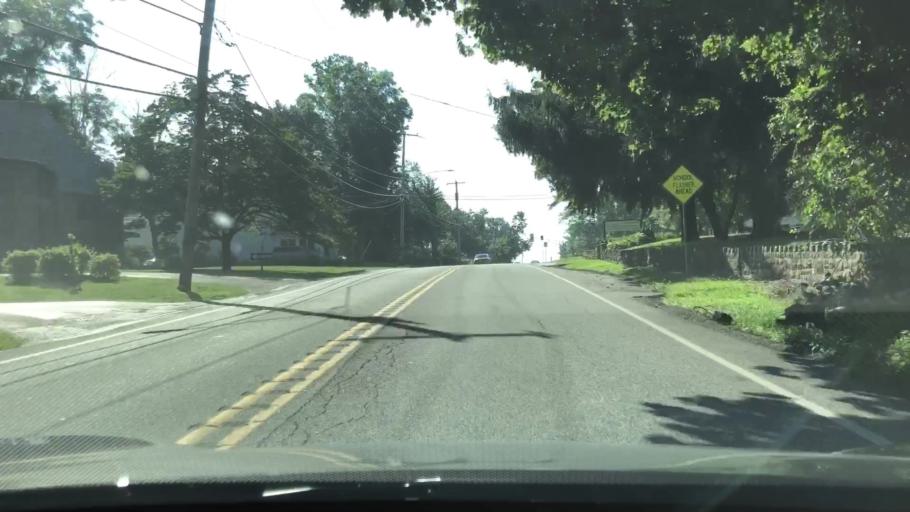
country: US
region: Pennsylvania
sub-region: Montgomery County
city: Dresher
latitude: 40.1534
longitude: -75.1731
